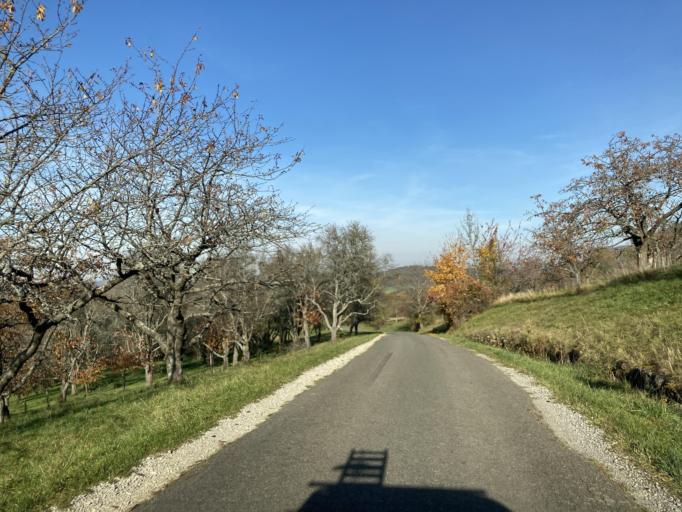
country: DE
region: Baden-Wuerttemberg
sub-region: Tuebingen Region
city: Mossingen
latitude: 48.3922
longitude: 9.0577
